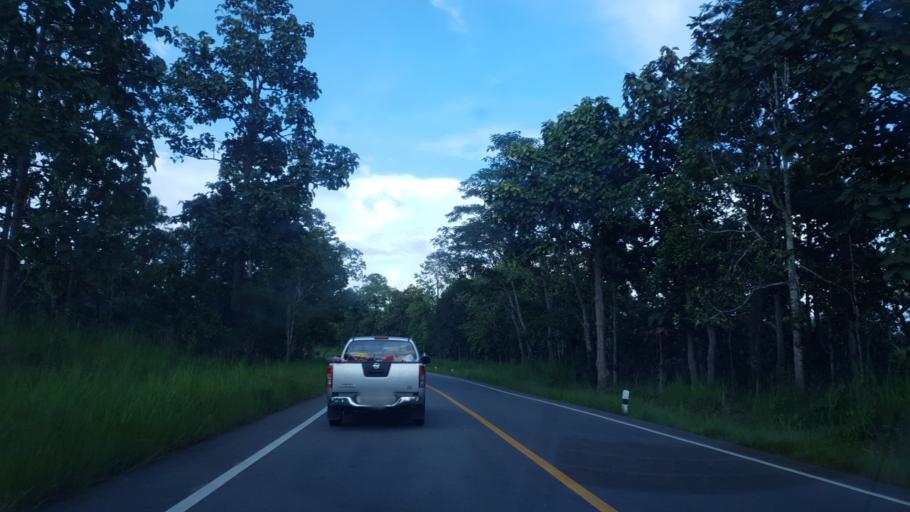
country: TH
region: Mae Hong Son
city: Khun Yuam
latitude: 18.7589
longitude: 97.9314
